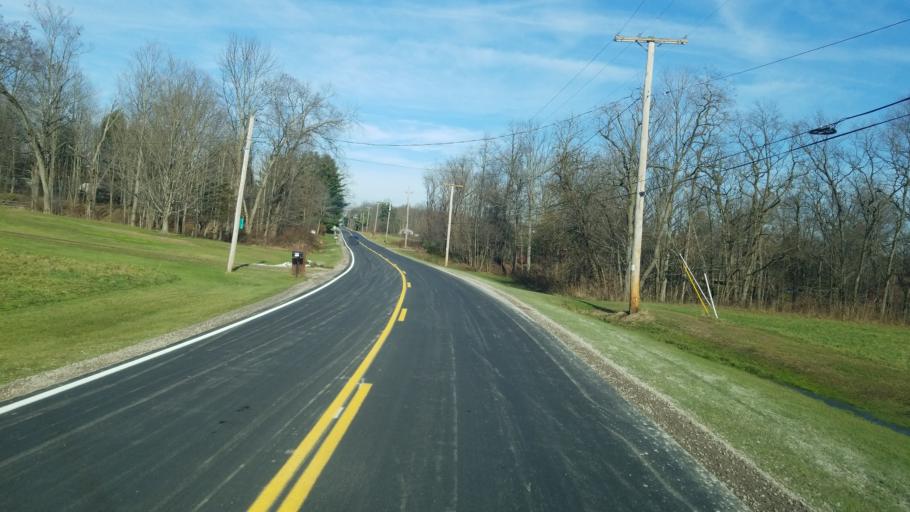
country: US
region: Ohio
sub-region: Ashtabula County
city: Roaming Shores
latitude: 41.6906
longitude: -80.9040
